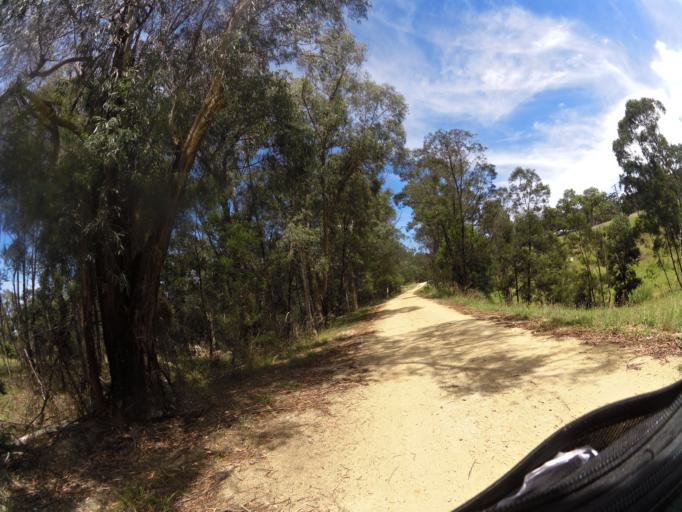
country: AU
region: Victoria
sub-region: East Gippsland
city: Lakes Entrance
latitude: -37.7310
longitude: 148.0878
